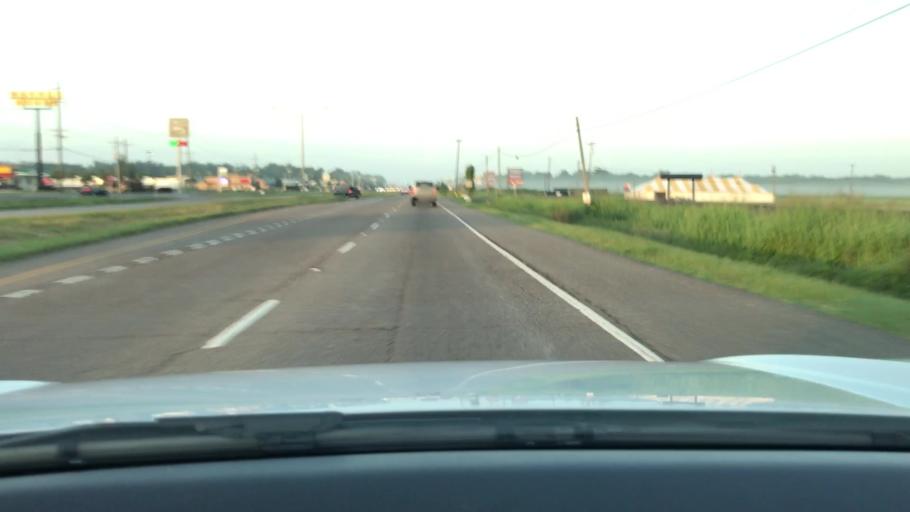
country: US
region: Louisiana
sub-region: West Baton Rouge Parish
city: Port Allen
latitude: 30.4254
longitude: -91.2166
